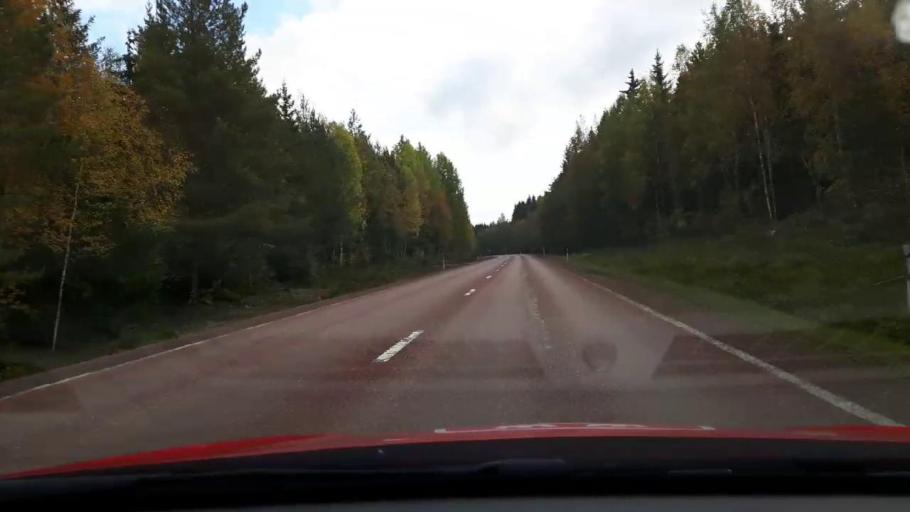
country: SE
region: Gaevleborg
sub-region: Ljusdals Kommun
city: Jaervsoe
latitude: 61.6401
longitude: 16.2351
